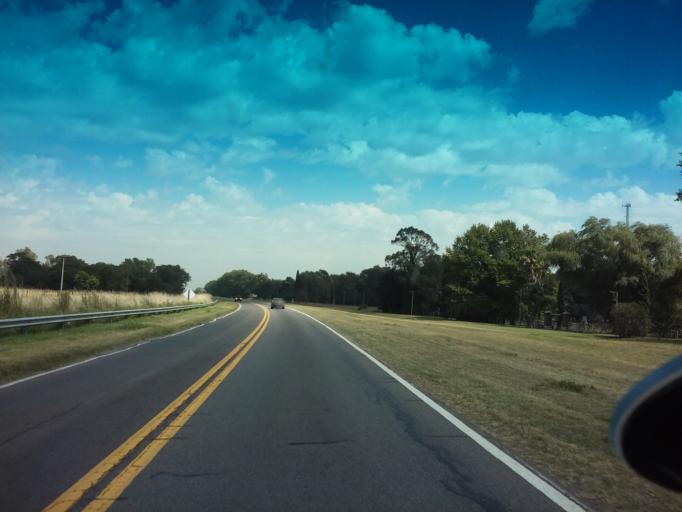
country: AR
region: Buenos Aires
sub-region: Partido de Carlos Casares
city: Carlos Casares
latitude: -35.6265
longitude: -61.3300
